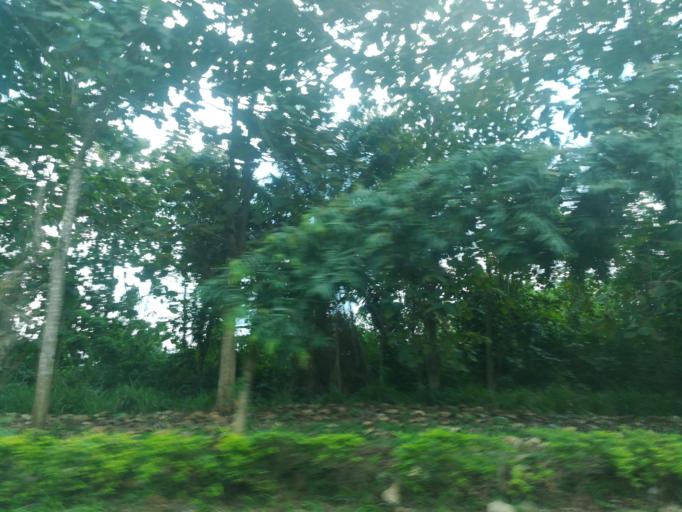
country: NG
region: Lagos
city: Ikorodu
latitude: 6.6408
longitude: 3.5218
